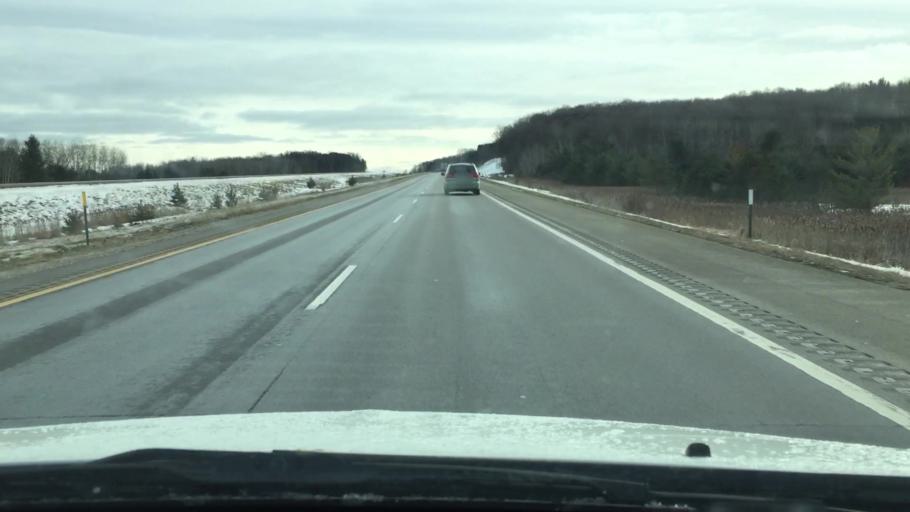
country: US
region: Michigan
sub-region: Wexford County
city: Manton
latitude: 44.4496
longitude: -85.3955
